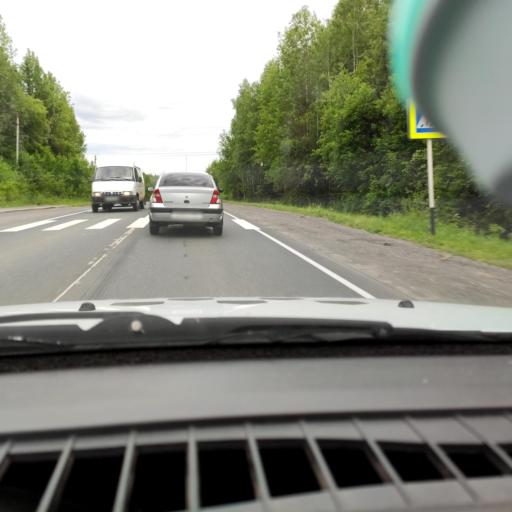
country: RU
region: Perm
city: Chusovoy
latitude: 58.2315
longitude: 57.8267
